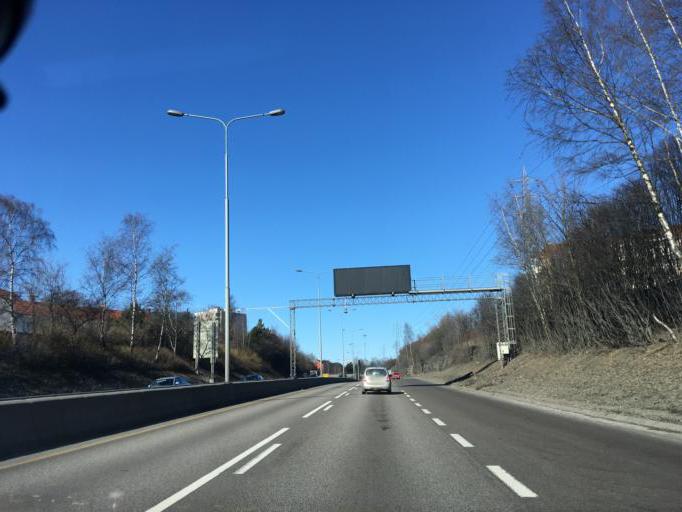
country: NO
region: Oslo
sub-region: Oslo
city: Oslo
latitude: 59.9146
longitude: 10.8149
